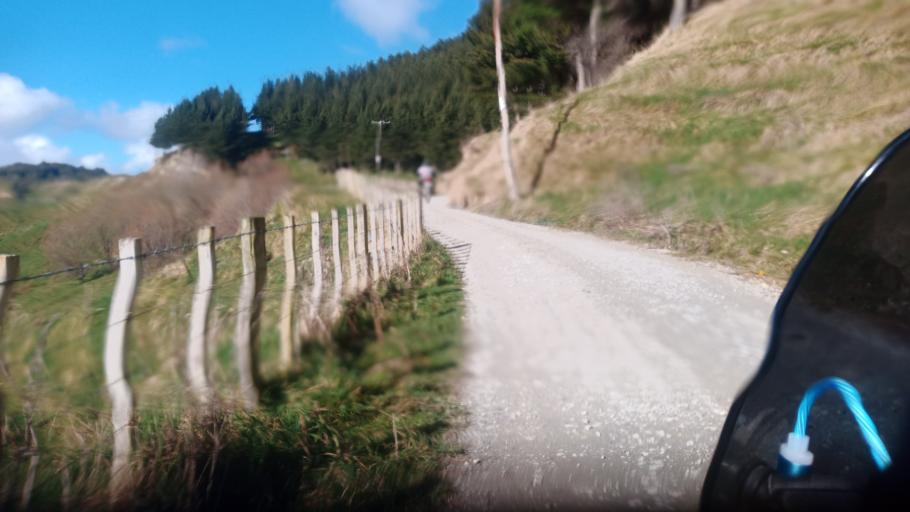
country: NZ
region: Hawke's Bay
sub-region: Wairoa District
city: Wairoa
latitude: -38.6650
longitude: 177.5184
